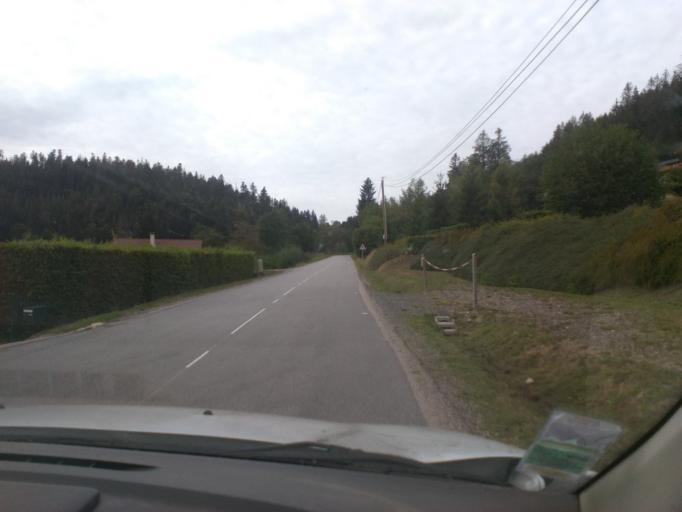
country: FR
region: Lorraine
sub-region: Departement des Vosges
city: Le Tholy
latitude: 48.0924
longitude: 6.7735
